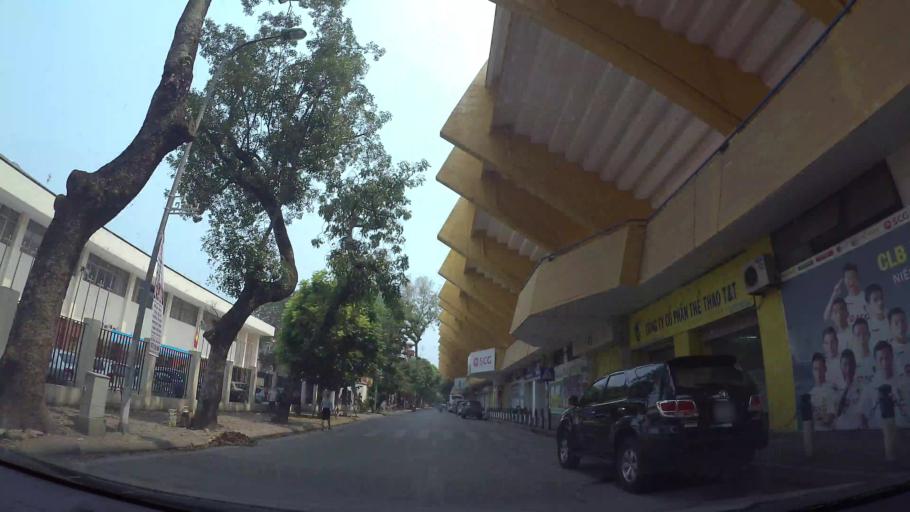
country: VN
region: Ha Noi
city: Dong Da
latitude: 21.0294
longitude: 105.8319
